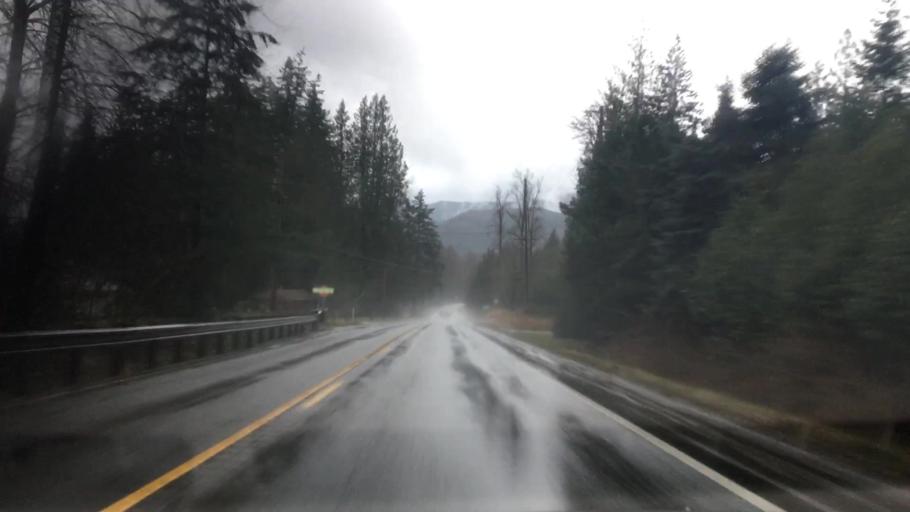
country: US
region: Washington
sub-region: Whatcom County
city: Peaceful Valley
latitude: 48.8278
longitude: -122.1782
